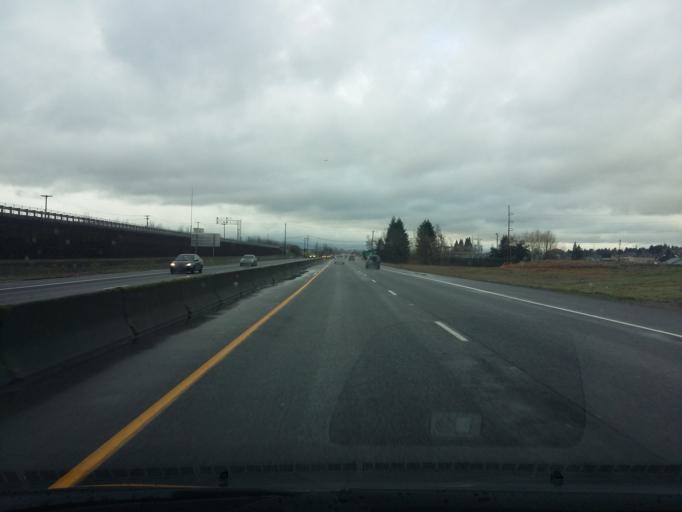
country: US
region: Washington
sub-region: Clark County
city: Vancouver
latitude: 45.6187
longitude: -122.6292
